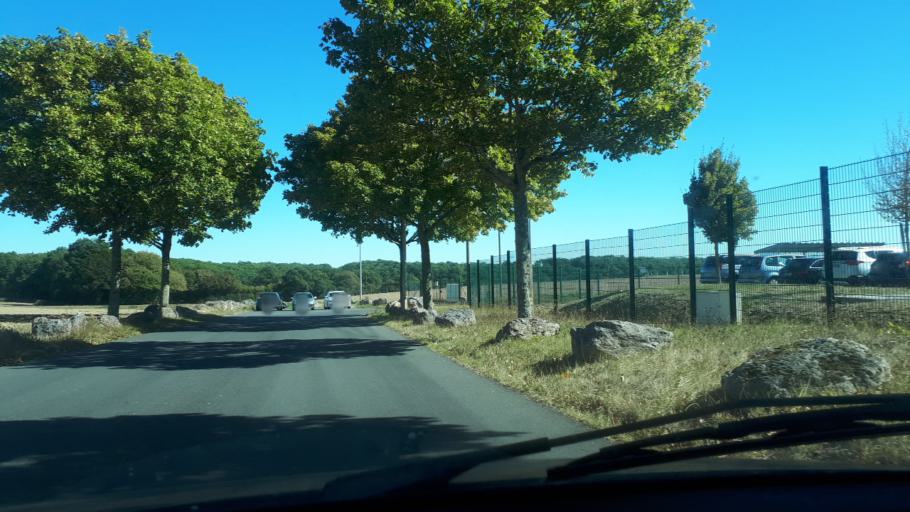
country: FR
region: Centre
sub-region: Departement du Loir-et-Cher
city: Naveil
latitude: 47.8119
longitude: 1.0286
